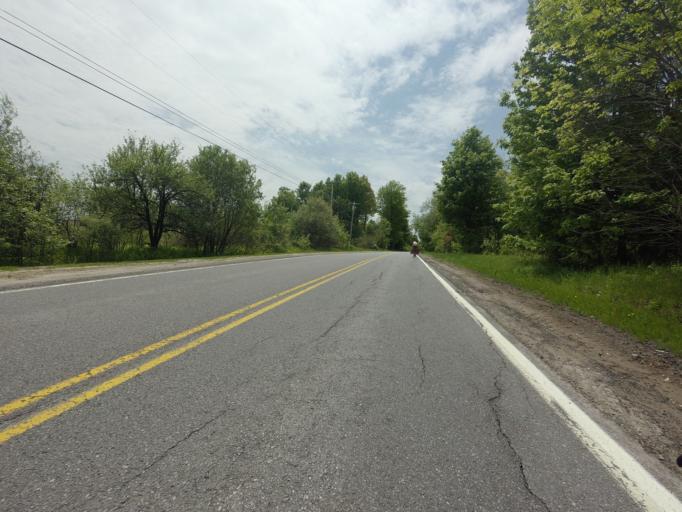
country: US
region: New York
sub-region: St. Lawrence County
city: Hannawa Falls
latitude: 44.5452
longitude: -75.0072
